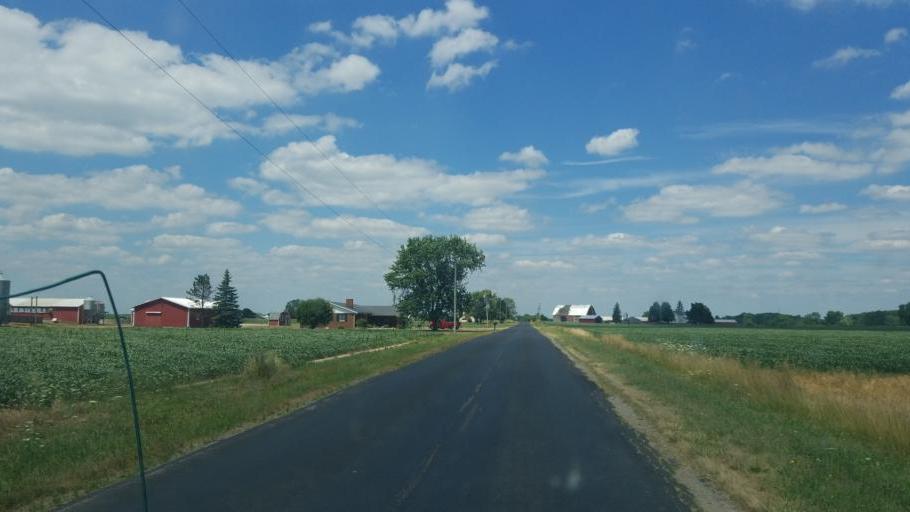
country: US
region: Ohio
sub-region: Williams County
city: Edgerton
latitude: 41.4594
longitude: -84.7104
